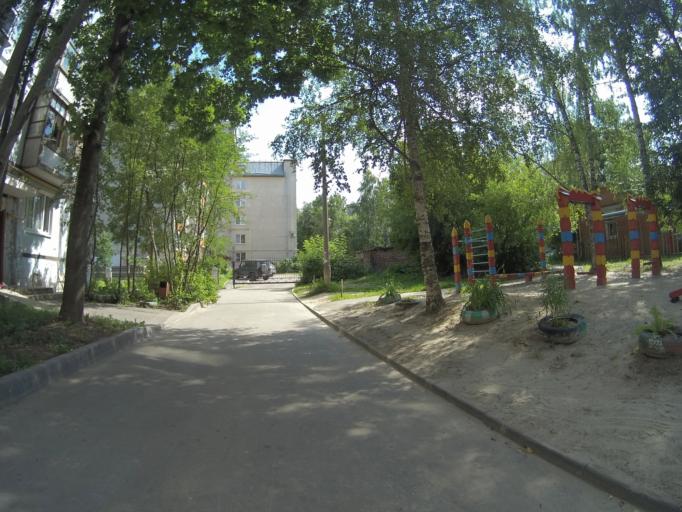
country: RU
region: Vladimir
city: Vladimir
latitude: 56.1221
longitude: 40.3724
